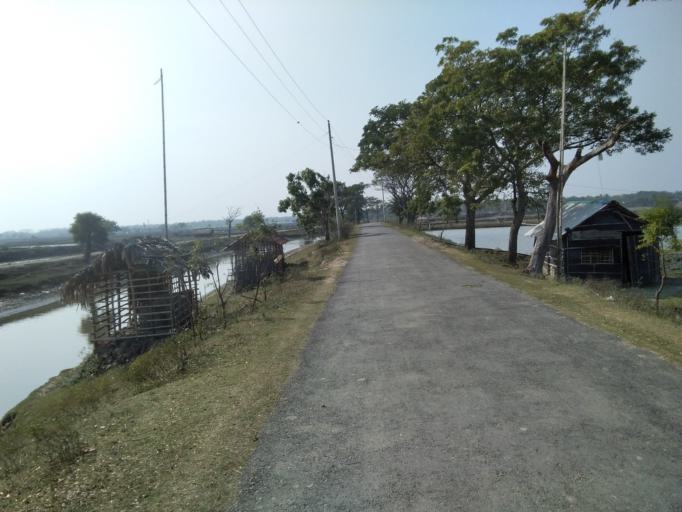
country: IN
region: West Bengal
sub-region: North 24 Parganas
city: Taki
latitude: 22.6356
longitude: 89.0069
